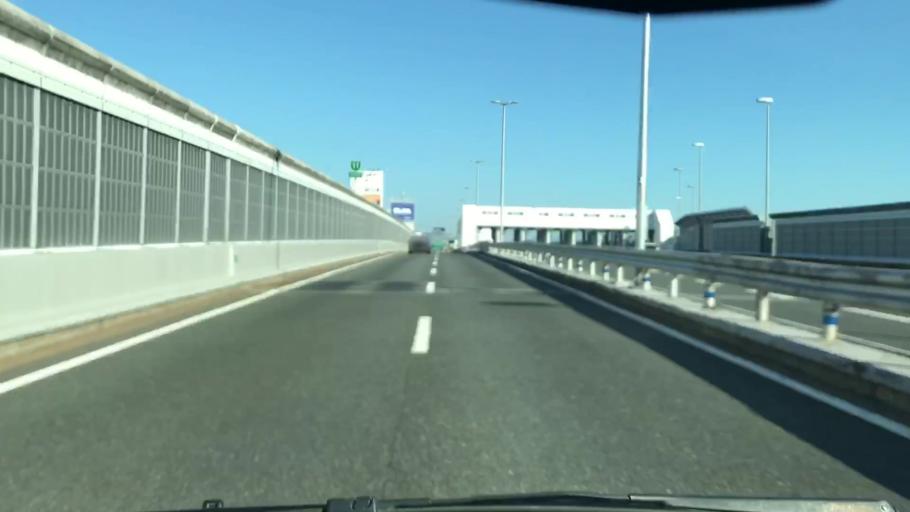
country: JP
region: Osaka
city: Toyonaka
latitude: 34.7828
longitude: 135.4528
